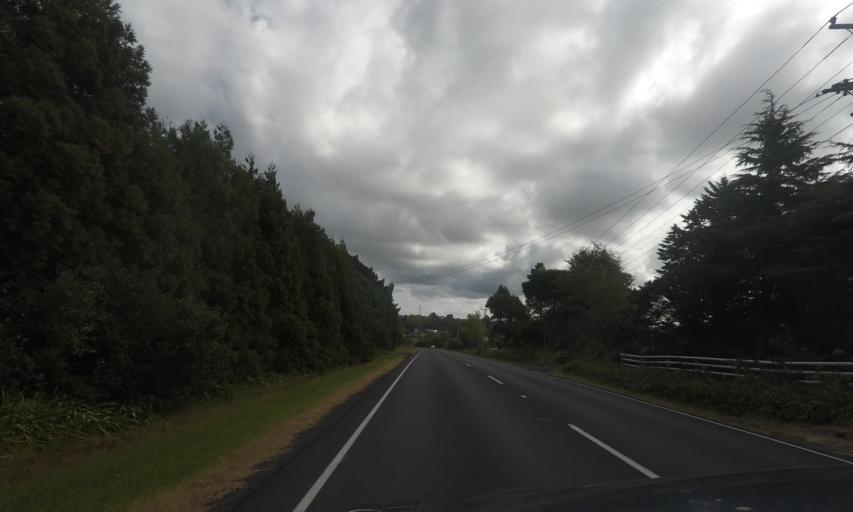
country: NZ
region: Auckland
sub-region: Auckland
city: Rosebank
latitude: -36.7942
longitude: 174.6059
